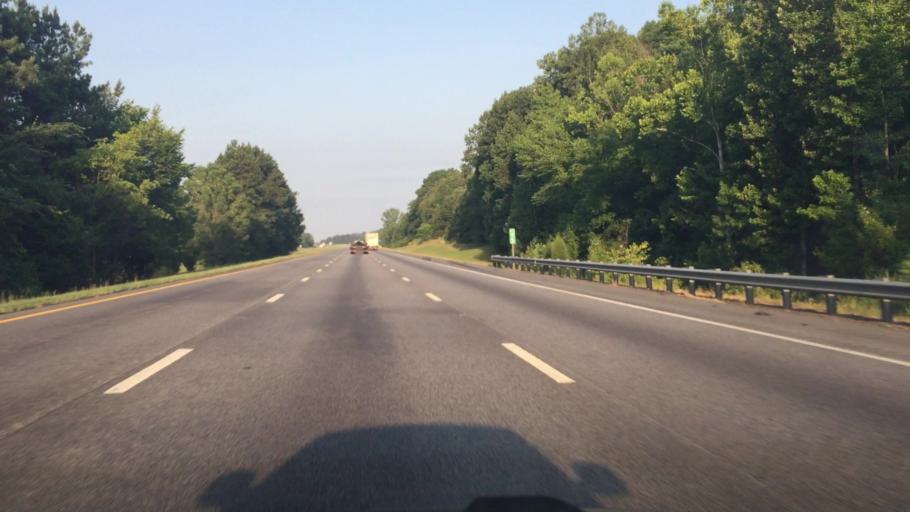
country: US
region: North Carolina
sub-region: Davidson County
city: Lexington
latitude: 35.8022
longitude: -80.1978
